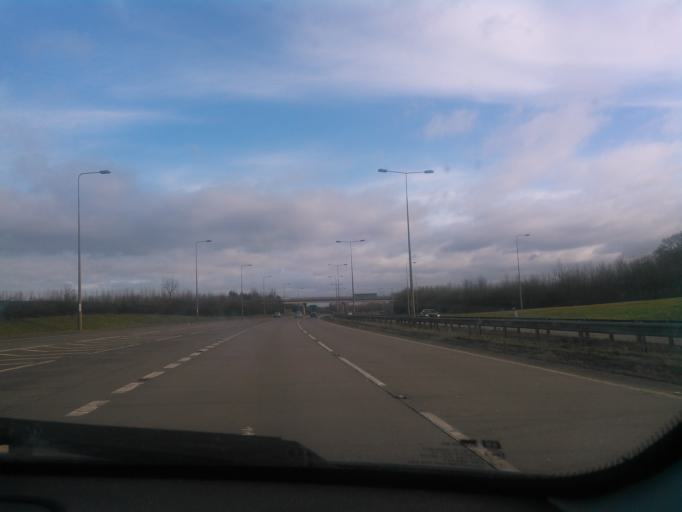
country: GB
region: England
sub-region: Derbyshire
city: Borrowash
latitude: 52.8715
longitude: -1.3911
